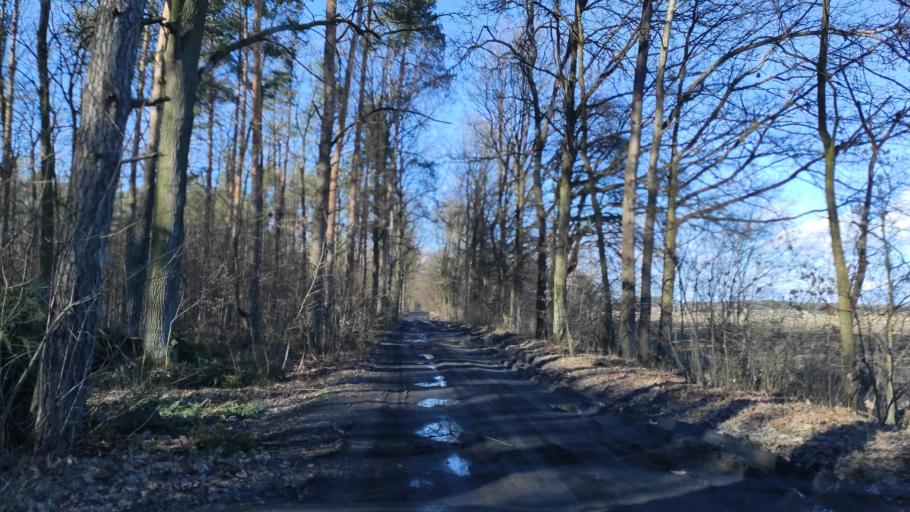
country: PL
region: Masovian Voivodeship
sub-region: Powiat radomski
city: Jedlnia-Letnisko
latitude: 51.4527
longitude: 21.3254
